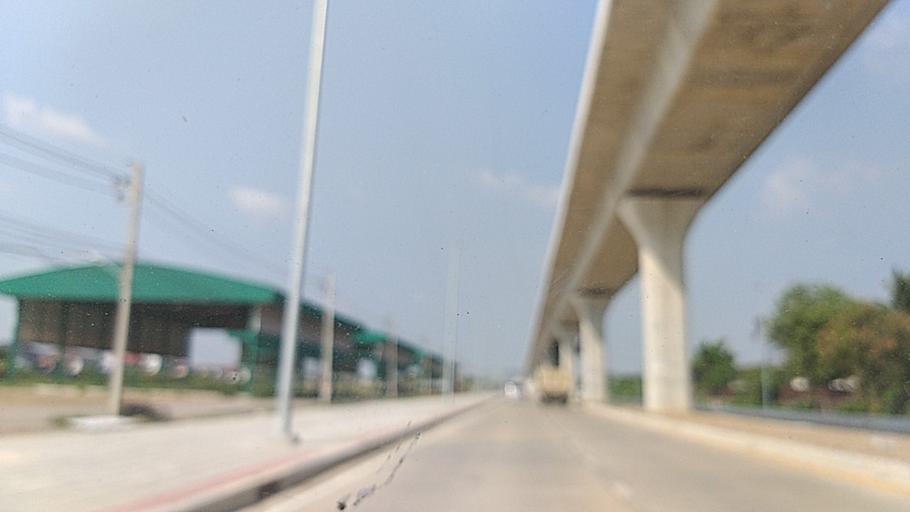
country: TH
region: Bangkok
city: Sai Mai
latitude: 13.9309
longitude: 100.6357
